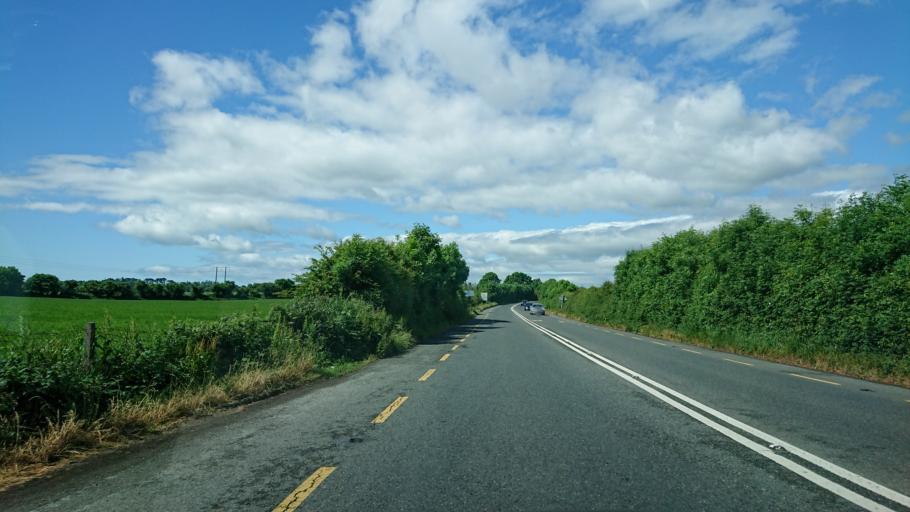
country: IE
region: Leinster
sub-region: Kilkenny
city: Mooncoin
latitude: 52.2331
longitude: -7.1934
